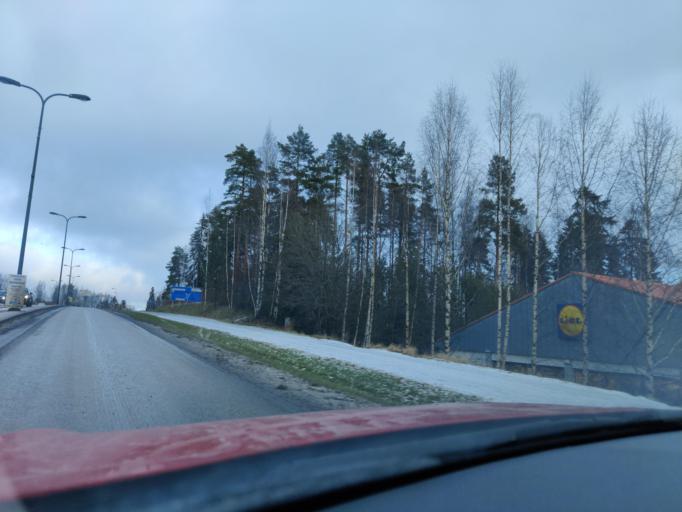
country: FI
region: Pirkanmaa
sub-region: Tampere
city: Nokia
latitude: 61.4664
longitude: 23.5046
